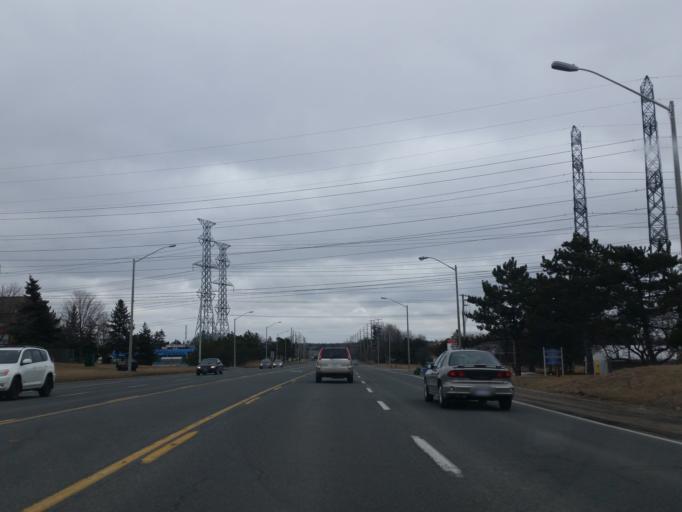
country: CA
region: Ontario
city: Ajax
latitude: 43.8433
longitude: -79.0808
